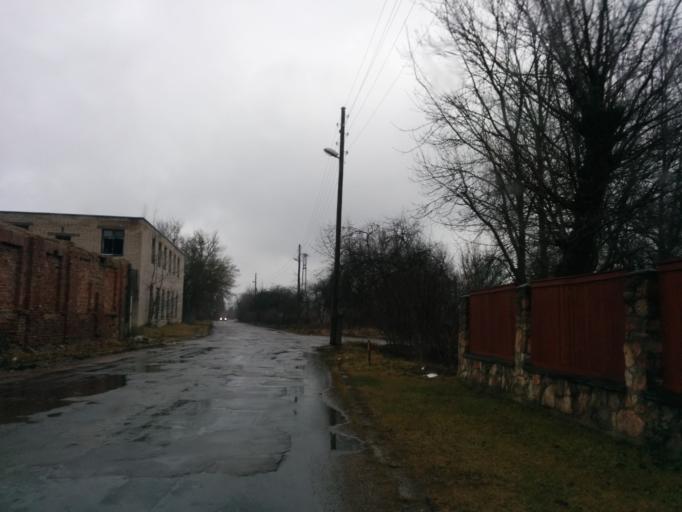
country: LV
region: Jelgava
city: Jelgava
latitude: 56.6610
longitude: 23.7186
